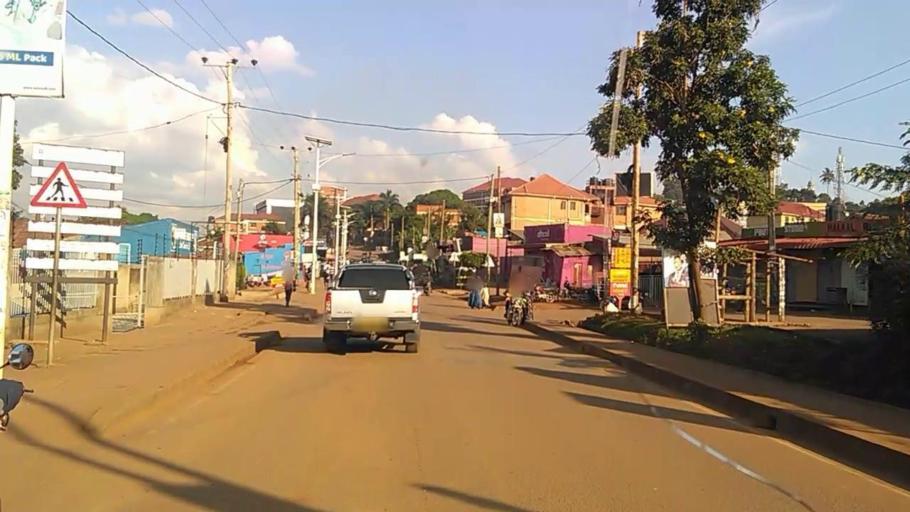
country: UG
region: Central Region
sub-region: Kampala District
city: Kampala
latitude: 0.3074
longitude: 32.5984
